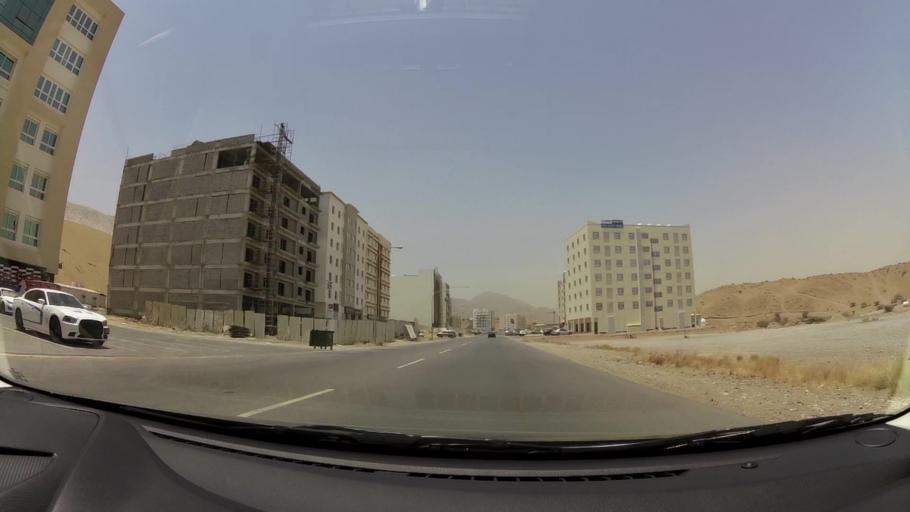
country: OM
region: Muhafazat Masqat
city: Bawshar
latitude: 23.5687
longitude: 58.4149
